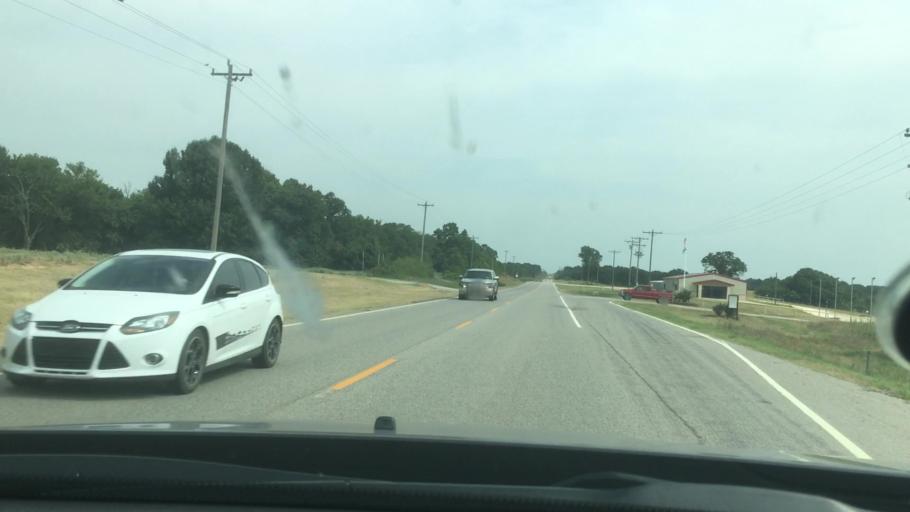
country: US
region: Oklahoma
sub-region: Bryan County
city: Durant
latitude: 34.2126
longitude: -96.4250
